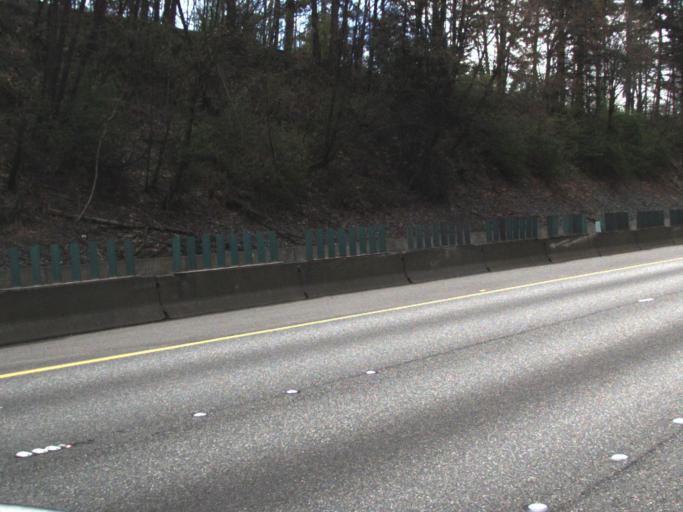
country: US
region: Washington
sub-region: King County
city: Lakeland South
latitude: 47.3022
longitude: -122.2773
